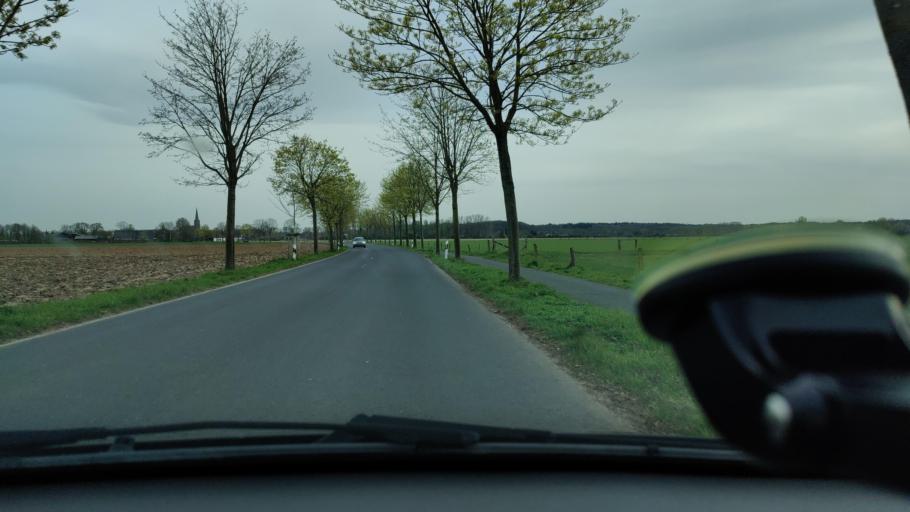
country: DE
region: North Rhine-Westphalia
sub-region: Regierungsbezirk Dusseldorf
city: Kleve
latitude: 51.7870
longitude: 6.1777
